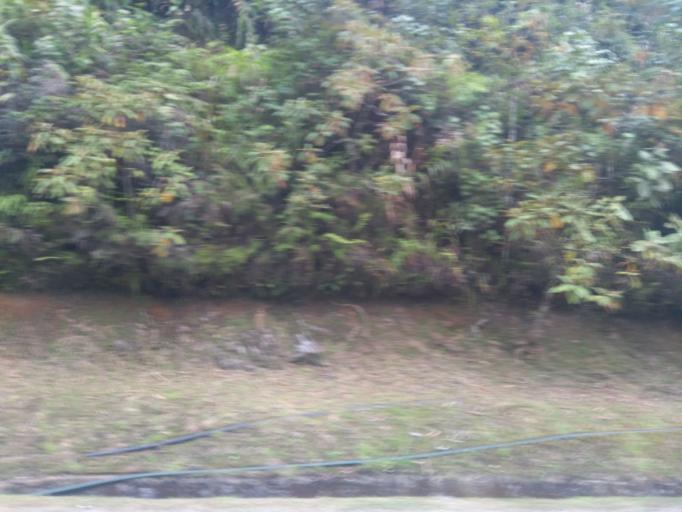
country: MY
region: Pahang
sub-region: Cameron Highlands
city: Tanah Rata
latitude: 4.5202
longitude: 101.4296
